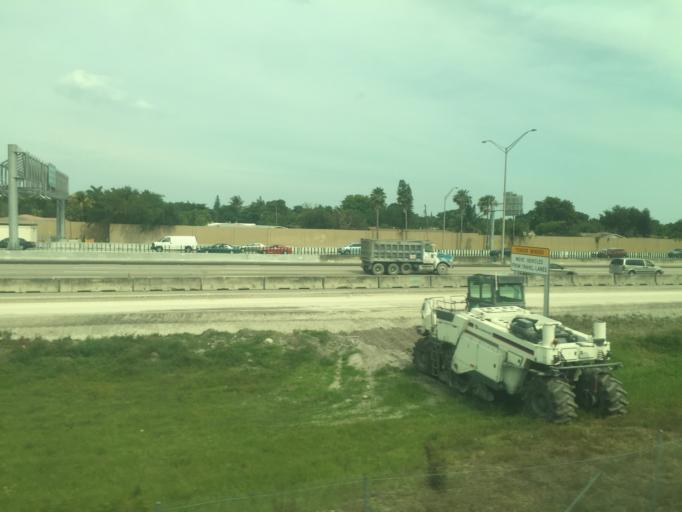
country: US
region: Florida
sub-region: Broward County
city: Hollywood
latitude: 26.0060
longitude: -80.1675
